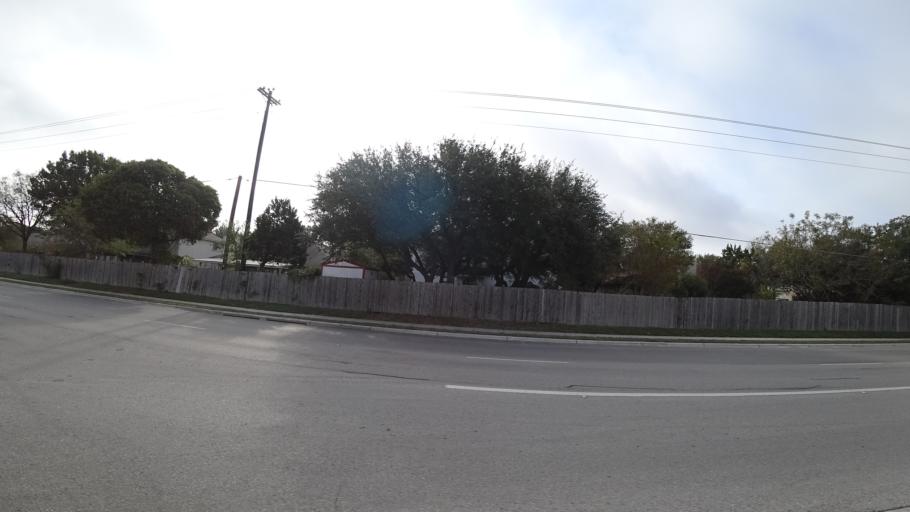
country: US
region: Texas
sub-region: Williamson County
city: Cedar Park
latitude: 30.5290
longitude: -97.8496
